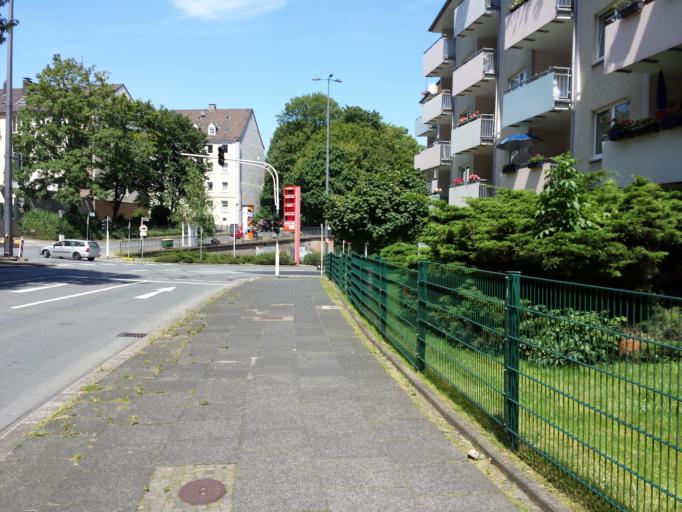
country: DE
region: North Rhine-Westphalia
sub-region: Regierungsbezirk Dusseldorf
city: Wuppertal
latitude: 51.2510
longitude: 7.1533
